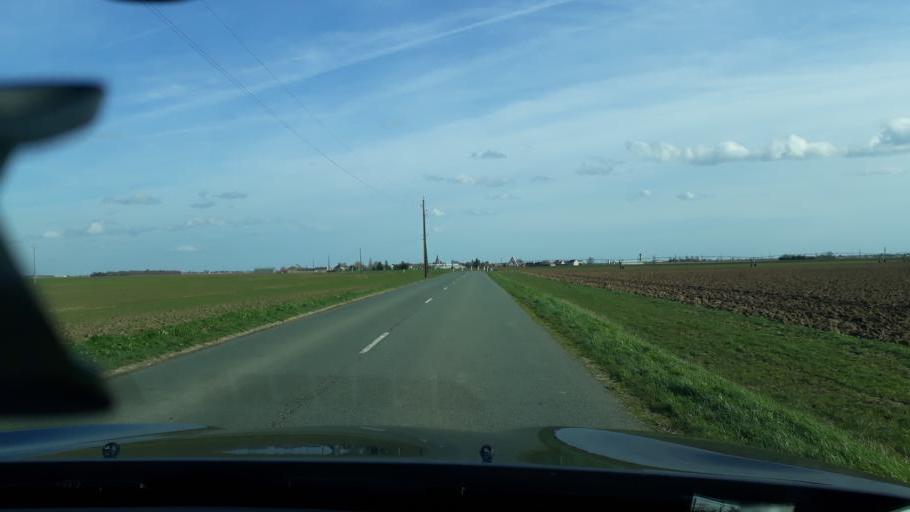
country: FR
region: Centre
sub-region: Departement du Loiret
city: Artenay
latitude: 48.0838
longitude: 1.9383
